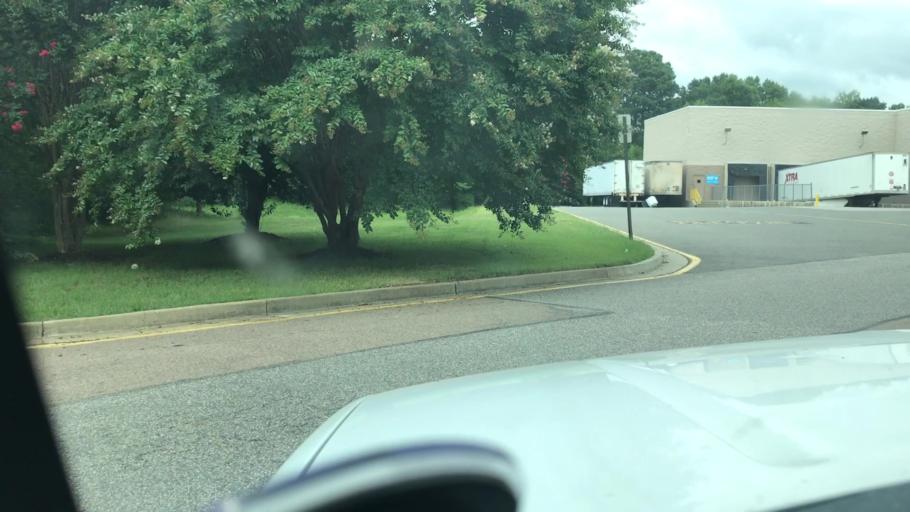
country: US
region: Virginia
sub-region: Henrico County
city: Laurel
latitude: 37.6415
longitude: -77.5584
